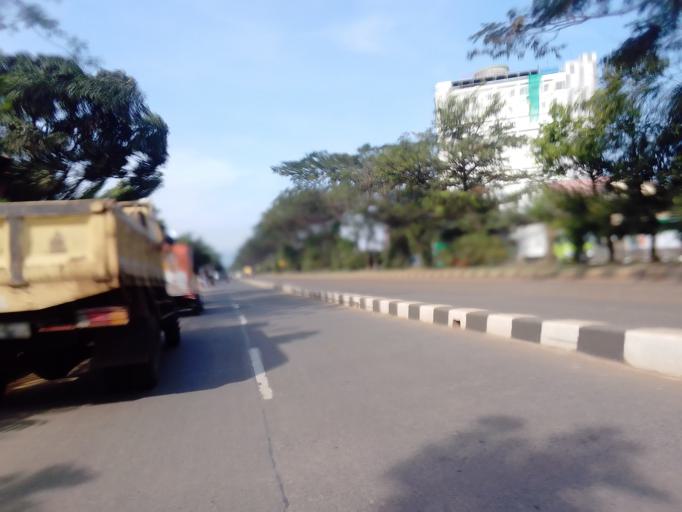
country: ID
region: West Java
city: Cileunyi
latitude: -6.9367
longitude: 107.6958
